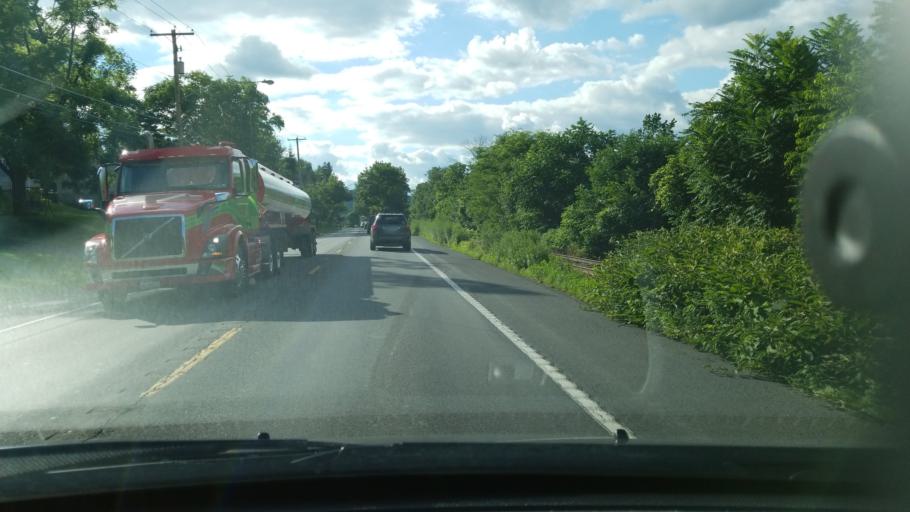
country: US
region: Pennsylvania
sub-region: Northumberland County
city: Riverside
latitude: 40.9531
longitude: -76.6193
